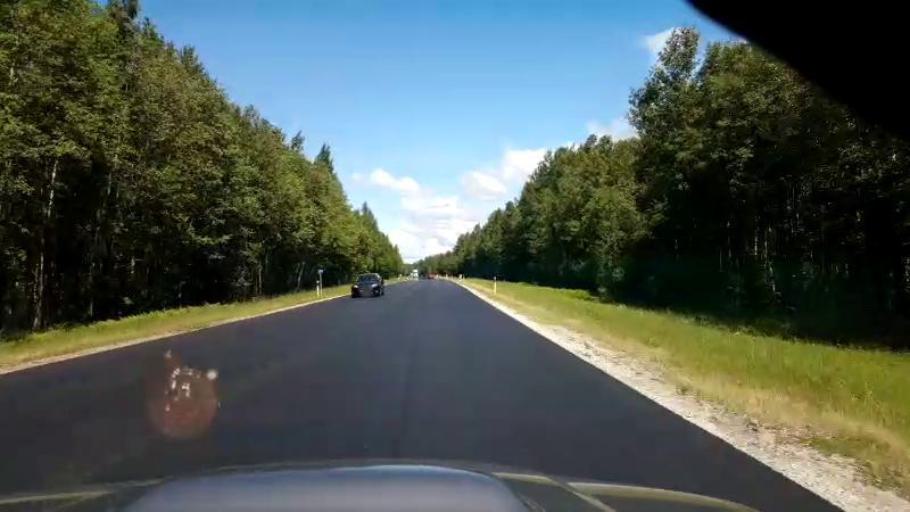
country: LV
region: Salacgrivas
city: Ainazi
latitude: 58.0212
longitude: 24.4993
